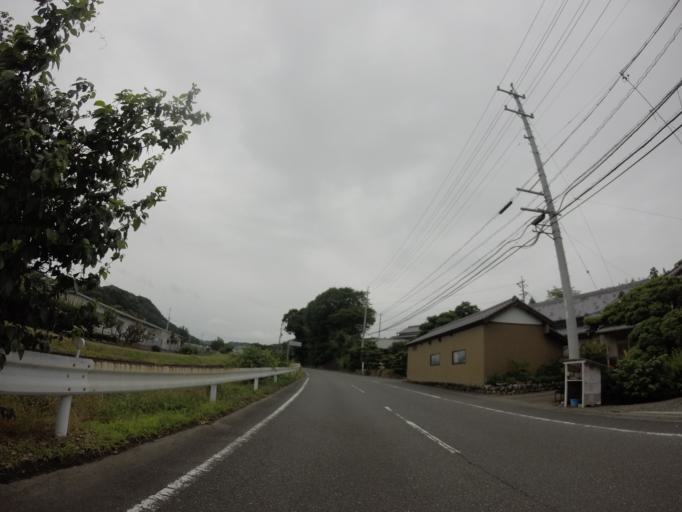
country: JP
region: Shizuoka
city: Shimada
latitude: 34.8043
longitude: 138.1865
